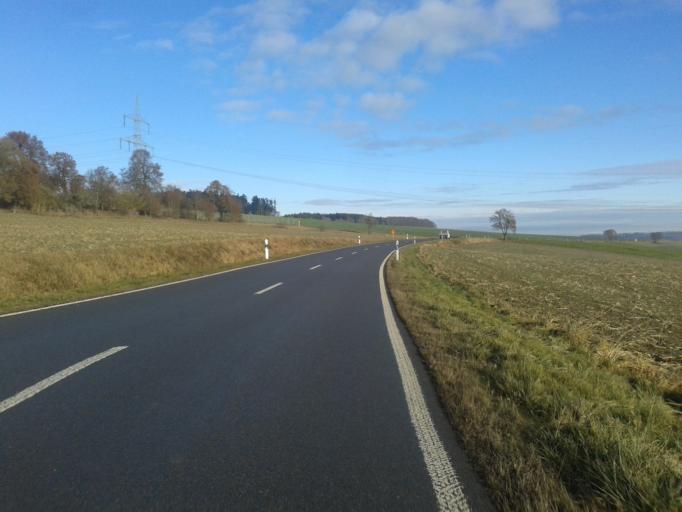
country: DE
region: Baden-Wuerttemberg
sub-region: Tuebingen Region
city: Blaubeuren
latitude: 48.3854
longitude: 9.8417
